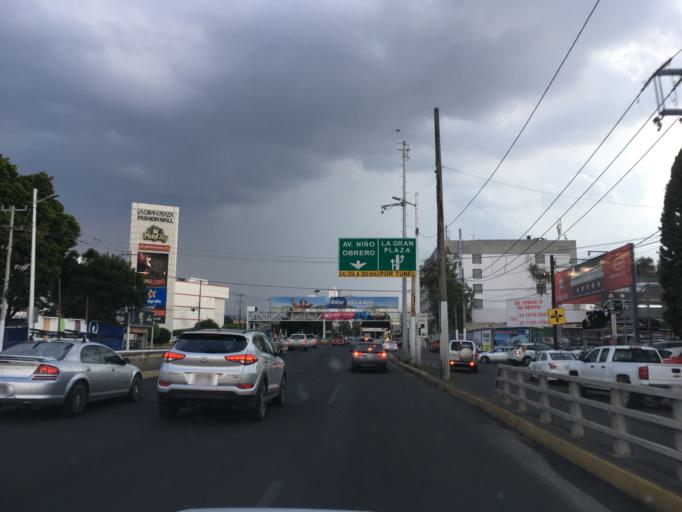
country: MX
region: Jalisco
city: Guadalajara
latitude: 20.6749
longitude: -103.4022
